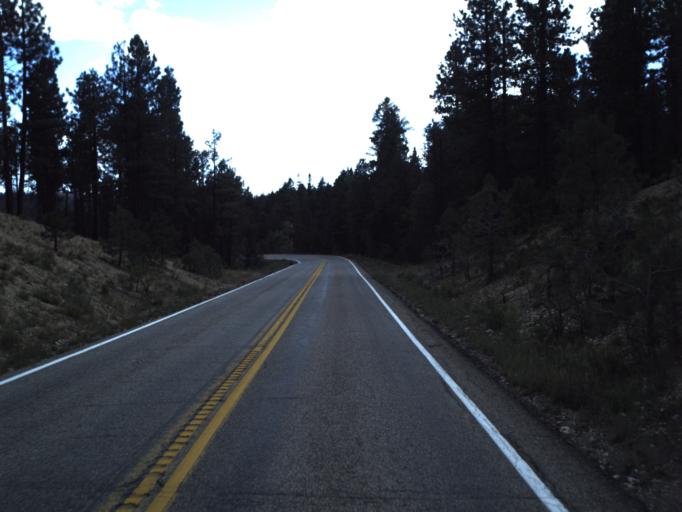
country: US
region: Utah
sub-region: Garfield County
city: Panguitch
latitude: 37.4953
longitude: -112.6205
